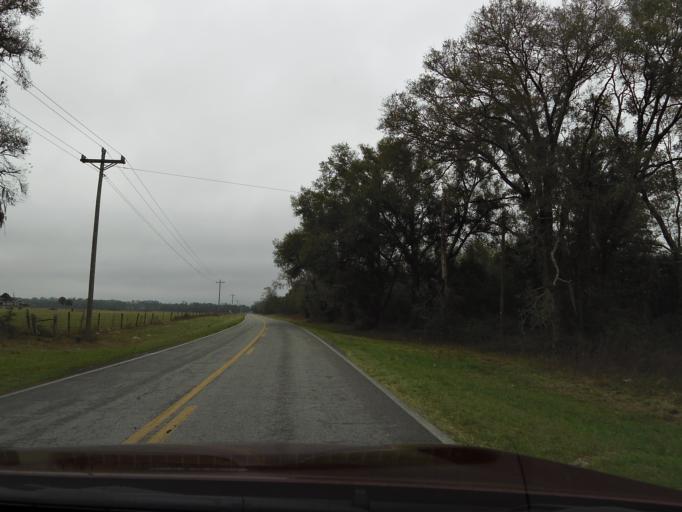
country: US
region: Florida
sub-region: Gilchrist County
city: Trenton
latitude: 29.8034
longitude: -82.9584
